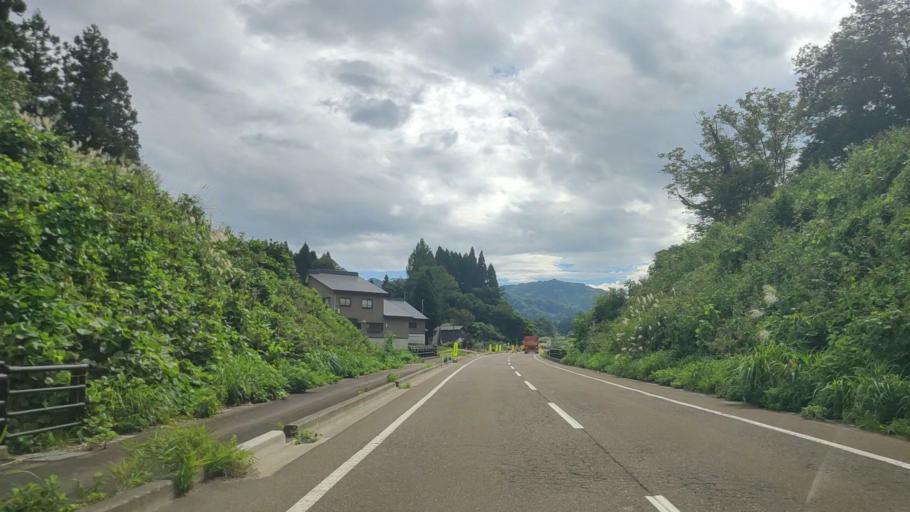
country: JP
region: Niigata
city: Arai
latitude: 36.9519
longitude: 138.2787
